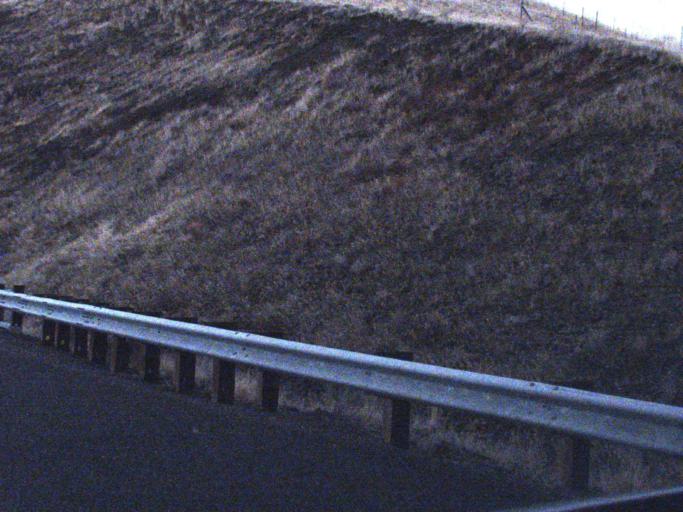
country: US
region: Washington
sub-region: Garfield County
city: Pomeroy
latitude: 46.6230
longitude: -117.7957
